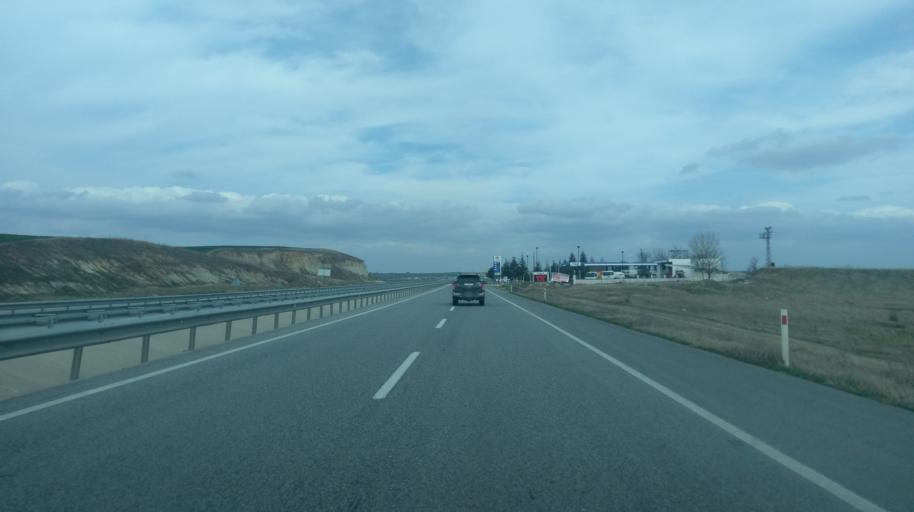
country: TR
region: Edirne
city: Kircasalih
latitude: 41.4080
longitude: 26.8174
